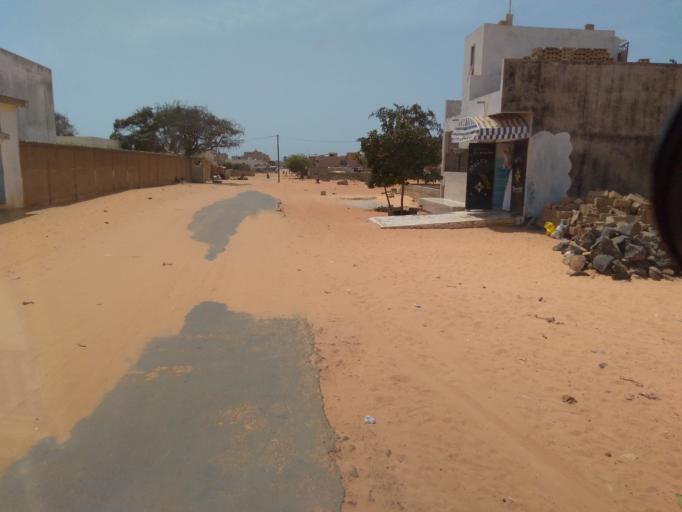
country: SN
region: Dakar
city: Pikine
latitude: 14.7861
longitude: -17.3350
